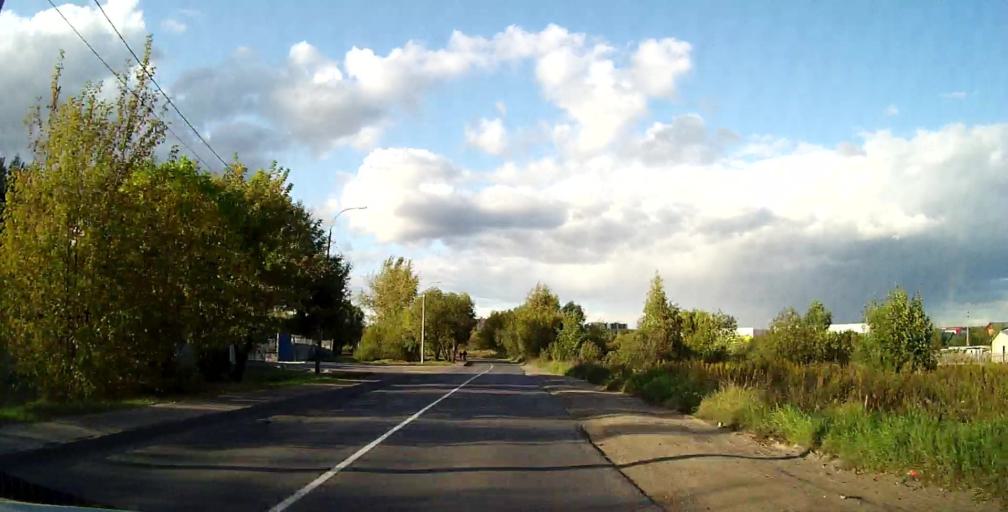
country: RU
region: Moskovskaya
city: Klimovsk
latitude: 55.3787
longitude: 37.5624
